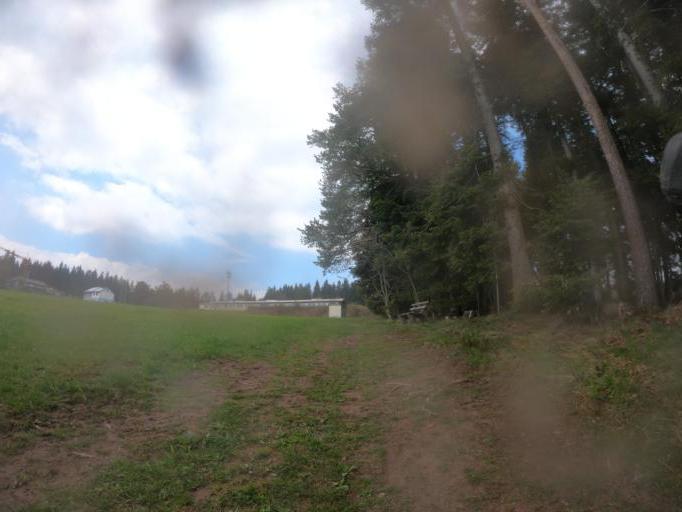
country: DE
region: Baden-Wuerttemberg
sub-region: Karlsruhe Region
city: Neuweiler
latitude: 48.6964
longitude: 8.5826
